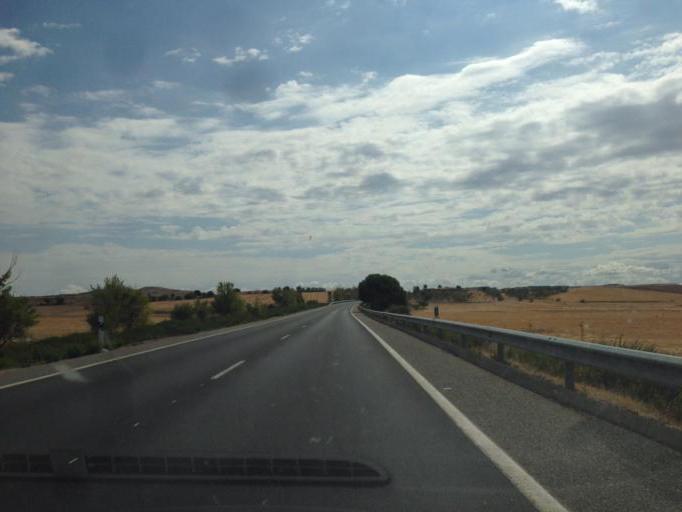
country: ES
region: Madrid
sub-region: Provincia de Madrid
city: Cobena
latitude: 40.5768
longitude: -3.5378
